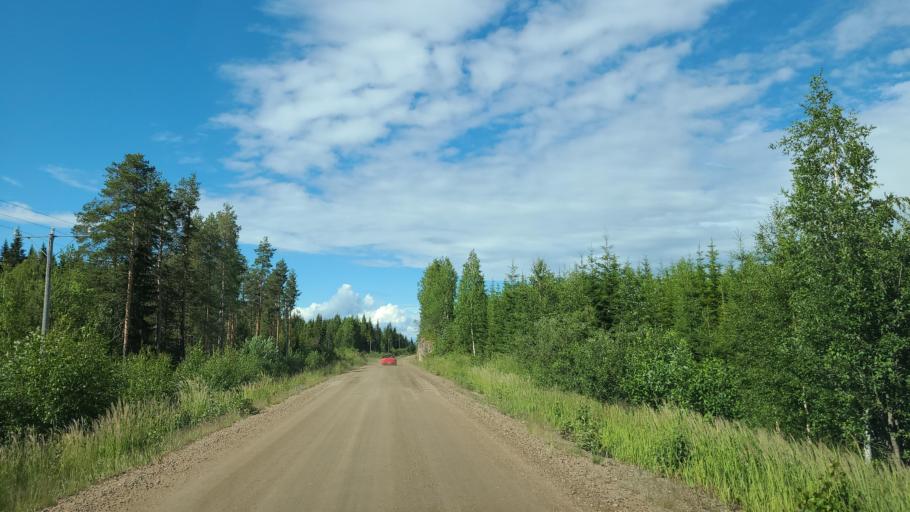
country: FI
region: Northern Savo
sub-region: Koillis-Savo
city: Kaavi
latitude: 62.9411
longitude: 28.7634
